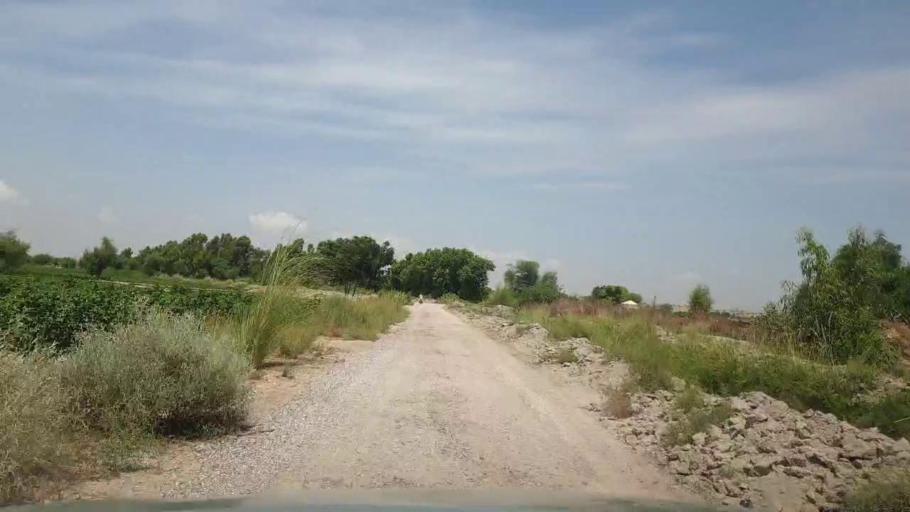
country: PK
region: Sindh
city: Bozdar
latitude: 27.0892
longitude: 69.0076
